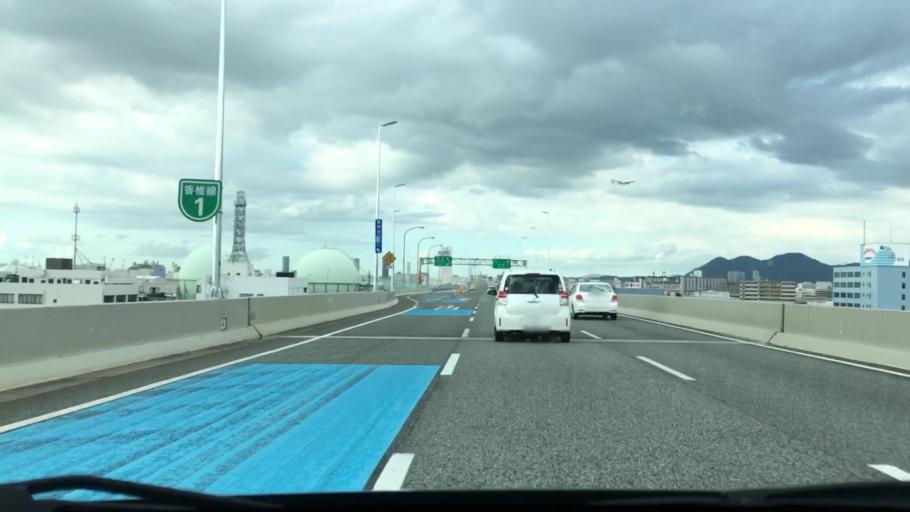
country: JP
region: Fukuoka
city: Fukuoka-shi
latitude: 33.6132
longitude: 130.4102
